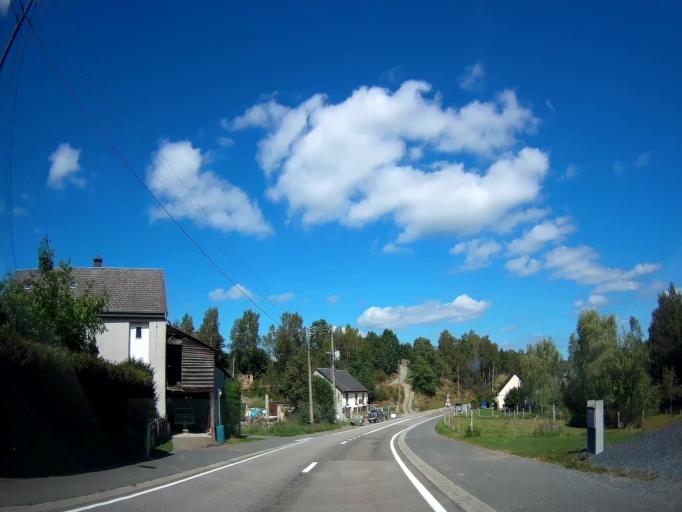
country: BE
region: Wallonia
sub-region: Province du Luxembourg
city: Bertogne
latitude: 50.0870
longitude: 5.6700
